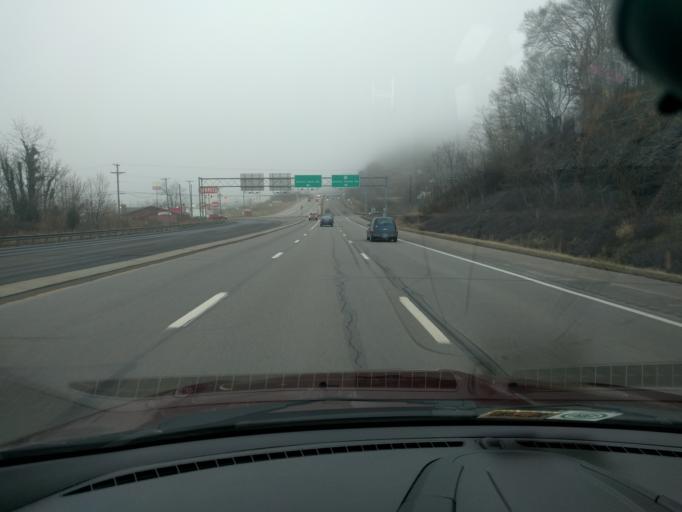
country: US
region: West Virginia
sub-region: Kanawha County
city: Chesapeake
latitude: 38.2029
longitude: -81.5012
